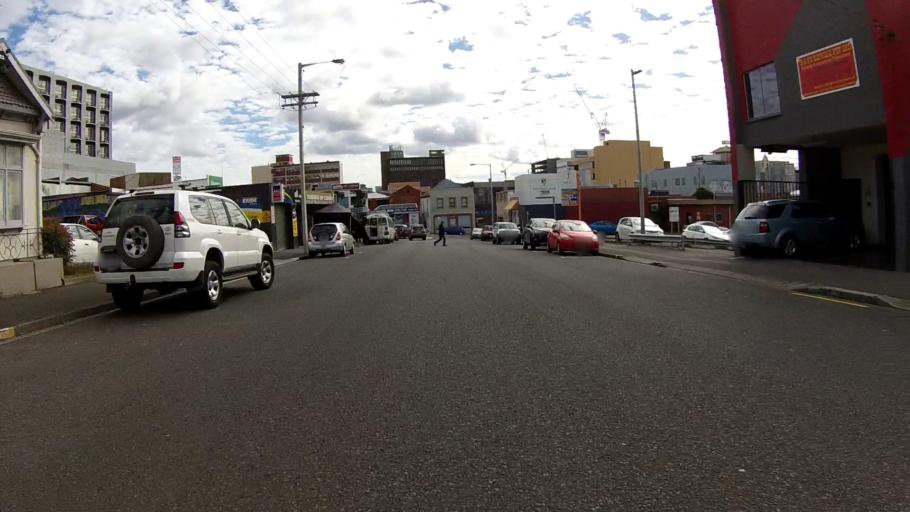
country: AU
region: Tasmania
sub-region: Hobart
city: Hobart
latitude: -42.8841
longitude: 147.3228
